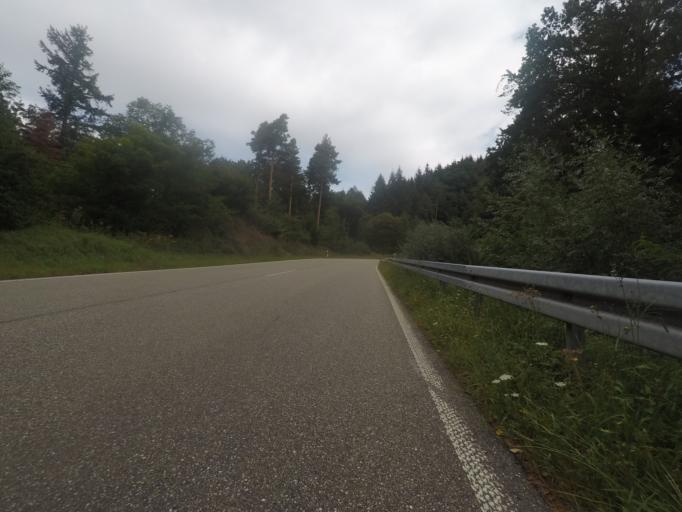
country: DE
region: Baden-Wuerttemberg
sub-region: Karlsruhe Region
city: Gaggenau
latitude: 48.8287
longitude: 8.3592
